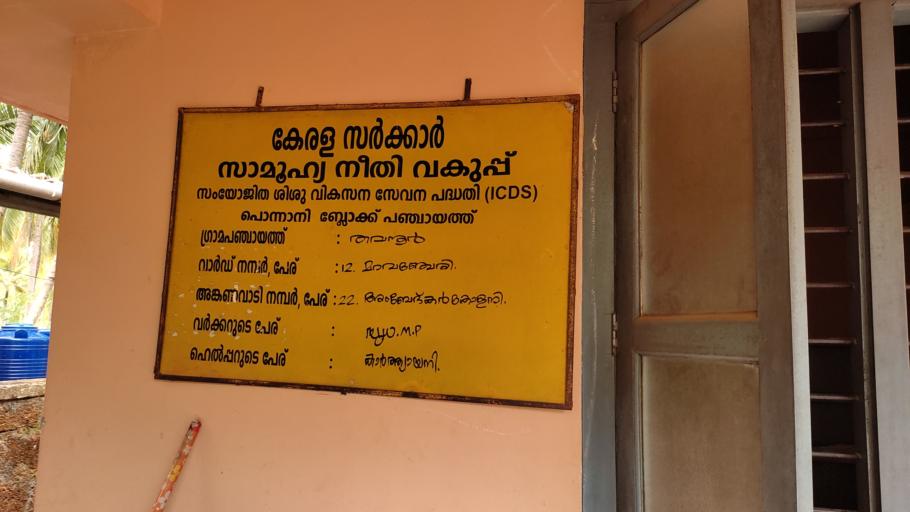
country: IN
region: Kerala
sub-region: Malappuram
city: Ponnani
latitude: 10.8311
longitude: 76.0010
